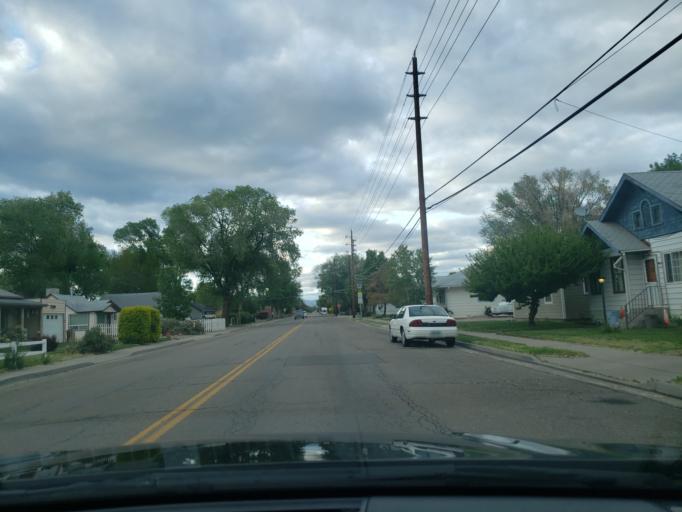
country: US
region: Colorado
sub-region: Mesa County
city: Fruita
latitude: 39.1595
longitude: -108.7290
